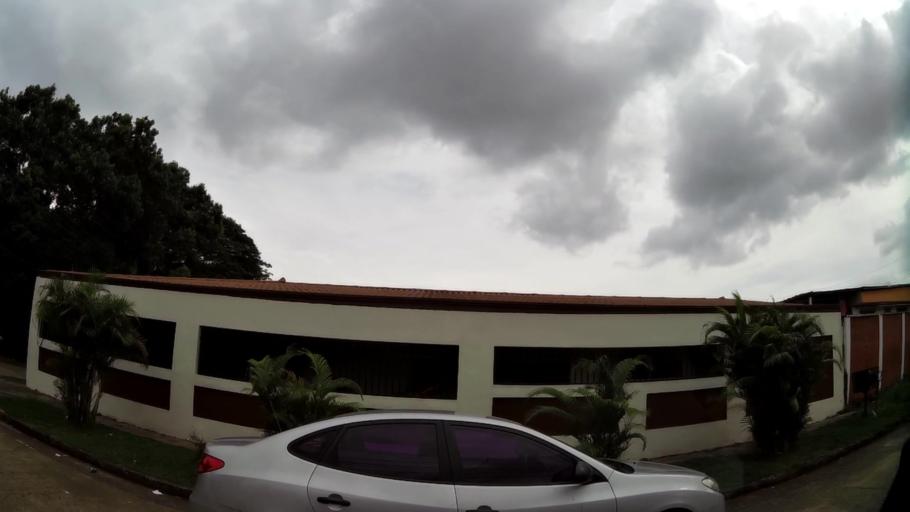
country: PA
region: Panama
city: Tocumen
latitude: 9.0570
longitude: -79.4102
